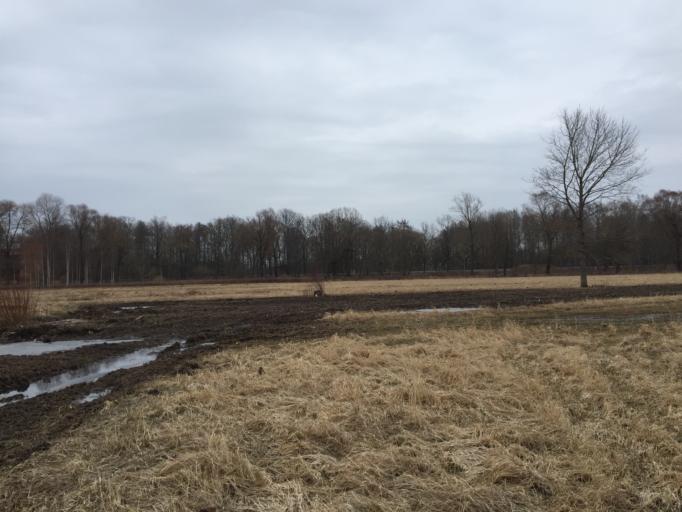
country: LV
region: Jelgava
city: Jelgava
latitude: 56.6837
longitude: 23.7173
